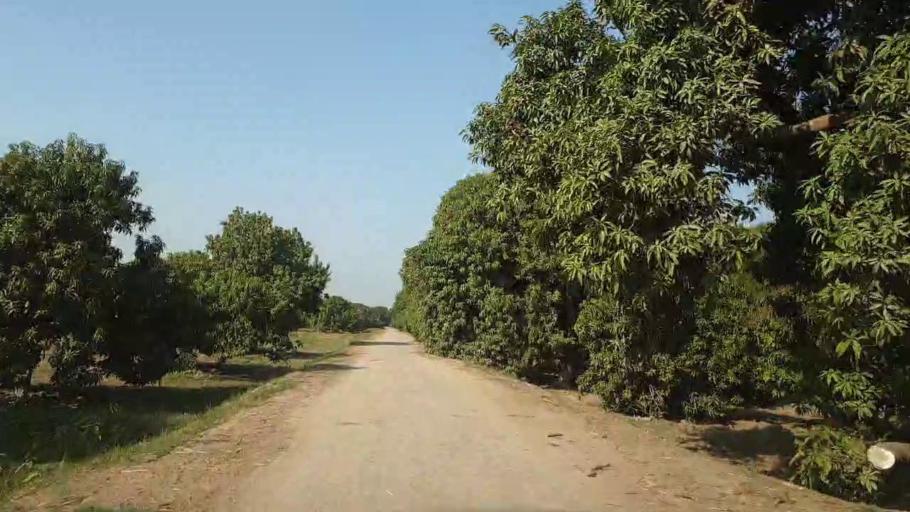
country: PK
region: Sindh
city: Tando Allahyar
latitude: 25.5717
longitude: 68.6722
